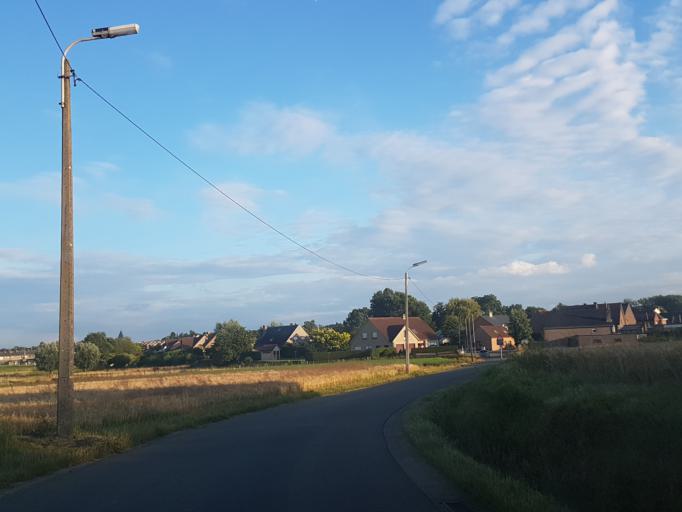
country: BE
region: Flanders
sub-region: Provincie Vlaams-Brabant
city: Opwijk
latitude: 50.9490
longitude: 4.1682
